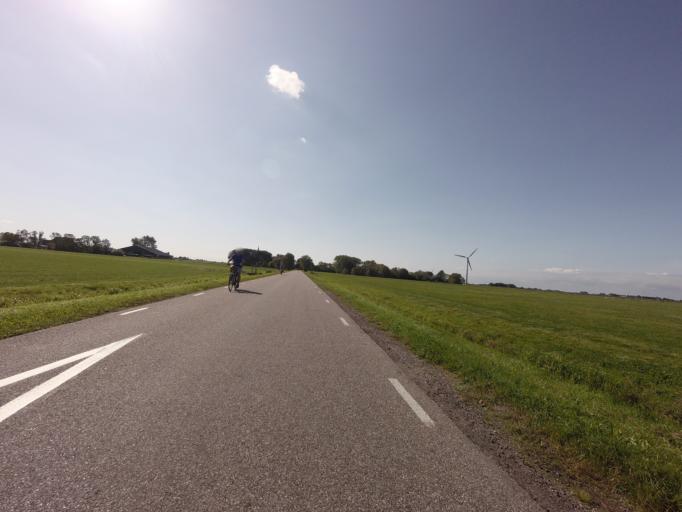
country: NL
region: Friesland
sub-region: Gemeente Littenseradiel
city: Makkum
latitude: 53.1147
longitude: 5.6816
